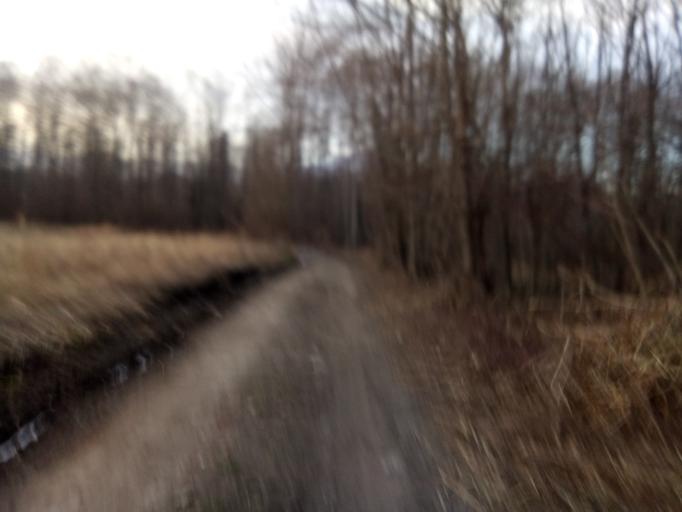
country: IT
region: Piedmont
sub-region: Provincia di Torino
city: Cascinette d'Ivrea
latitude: 45.4861
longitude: 7.9140
